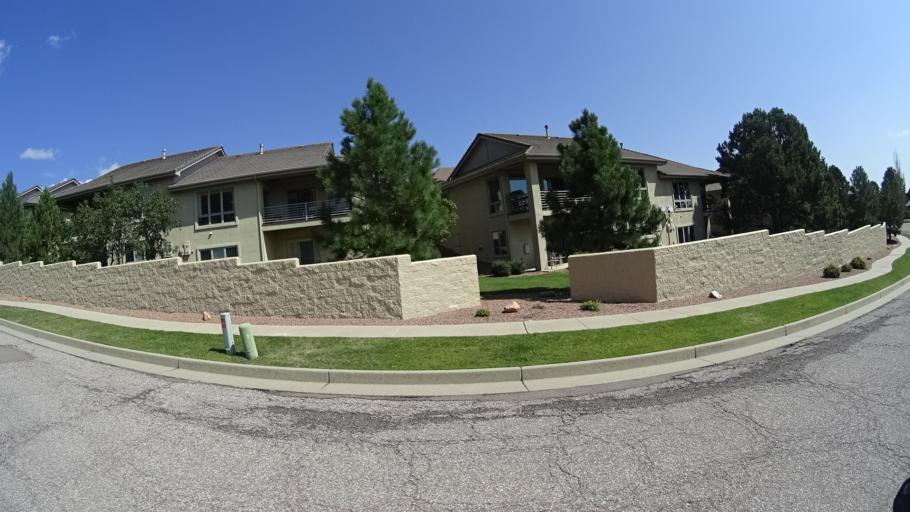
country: US
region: Colorado
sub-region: El Paso County
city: Manitou Springs
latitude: 38.9154
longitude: -104.8773
